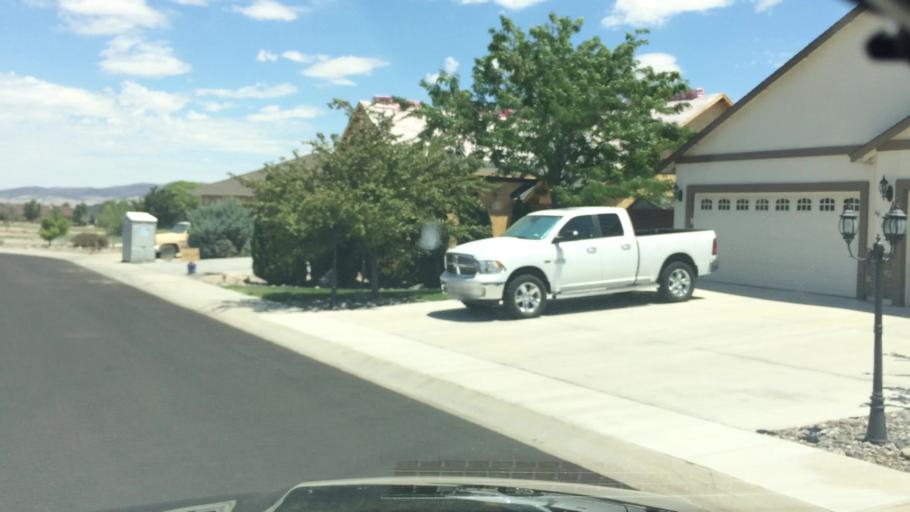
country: US
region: Nevada
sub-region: Lyon County
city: Fernley
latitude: 39.5835
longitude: -119.1414
